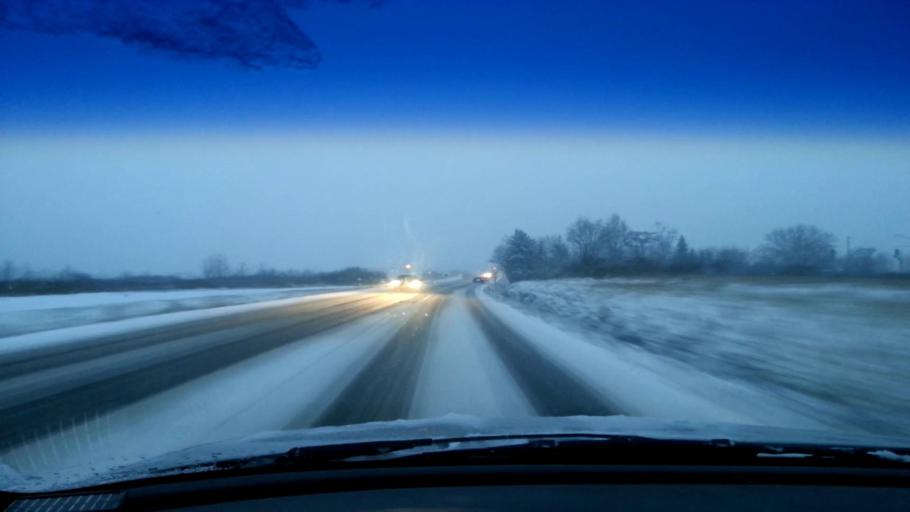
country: DE
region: Bavaria
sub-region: Upper Franconia
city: Kemmern
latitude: 49.9442
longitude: 10.8851
